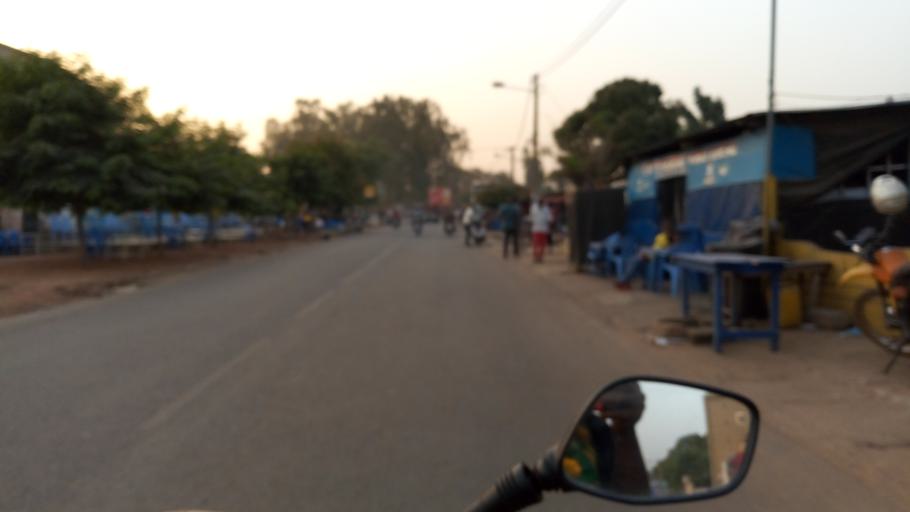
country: TG
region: Kara
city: Kara
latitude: 9.5493
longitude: 1.1853
